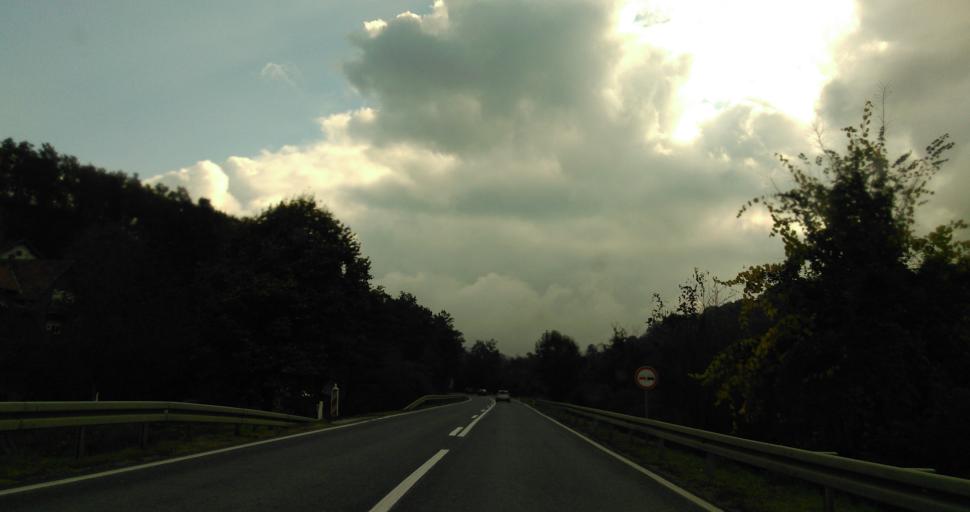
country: RS
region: Central Serbia
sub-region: Kolubarski Okrug
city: Ljig
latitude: 44.1867
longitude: 20.3399
